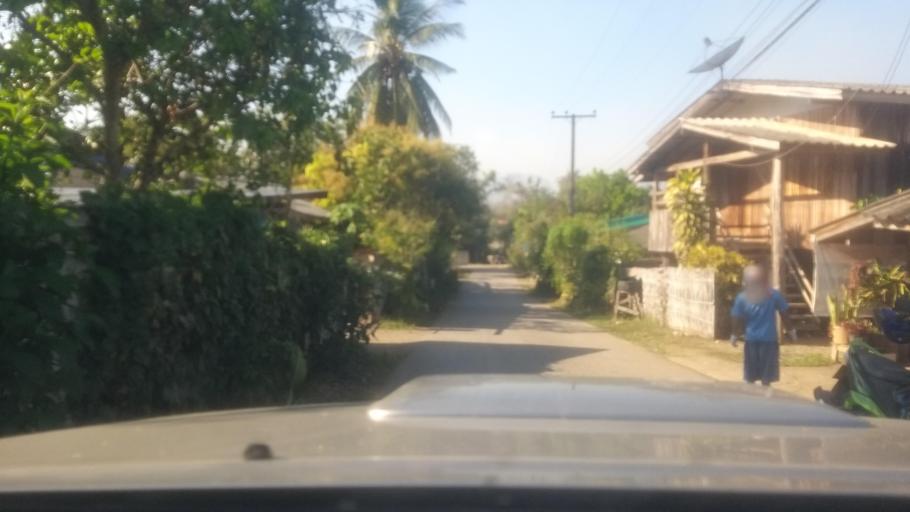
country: TH
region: Phrae
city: Phrae
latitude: 18.2580
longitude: 99.9865
